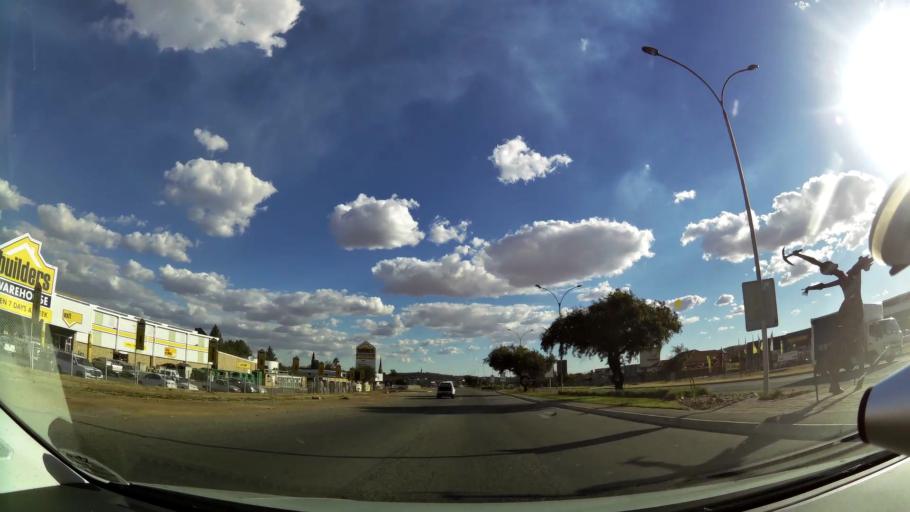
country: ZA
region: North-West
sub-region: Dr Kenneth Kaunda District Municipality
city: Klerksdorp
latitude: -26.8566
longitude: 26.6765
